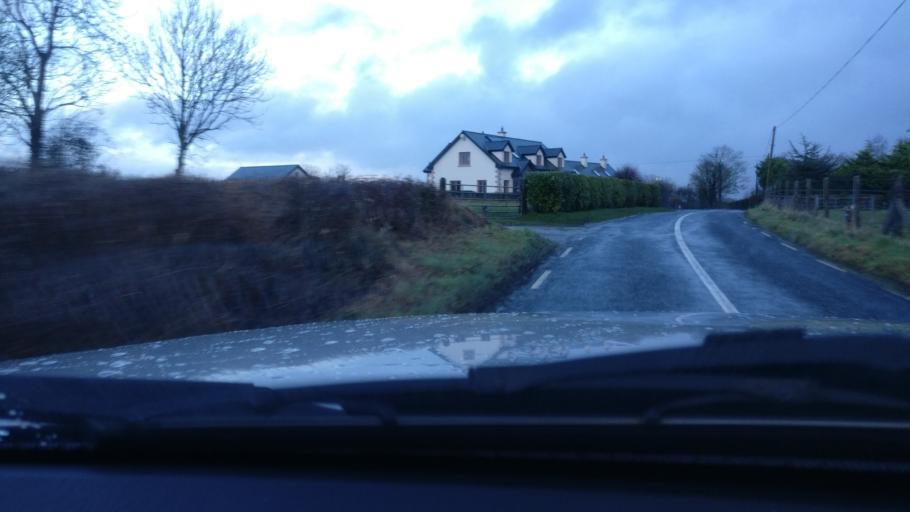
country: IE
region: Connaught
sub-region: County Galway
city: Ballinasloe
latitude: 53.2270
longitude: -8.3559
